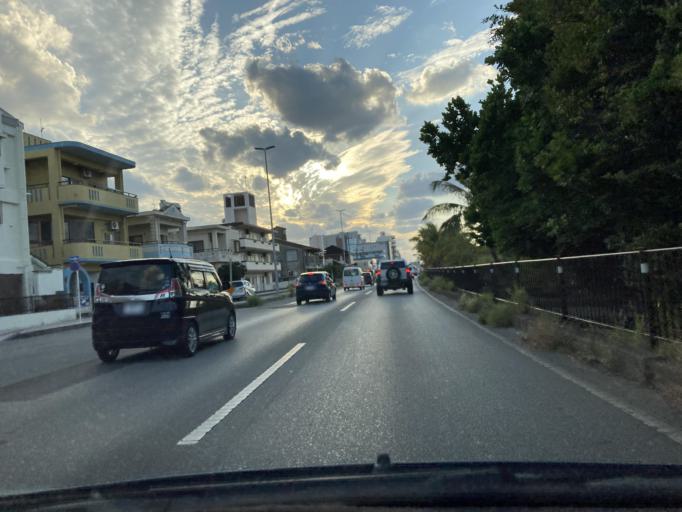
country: JP
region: Okinawa
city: Ginowan
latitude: 26.2799
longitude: 127.7396
